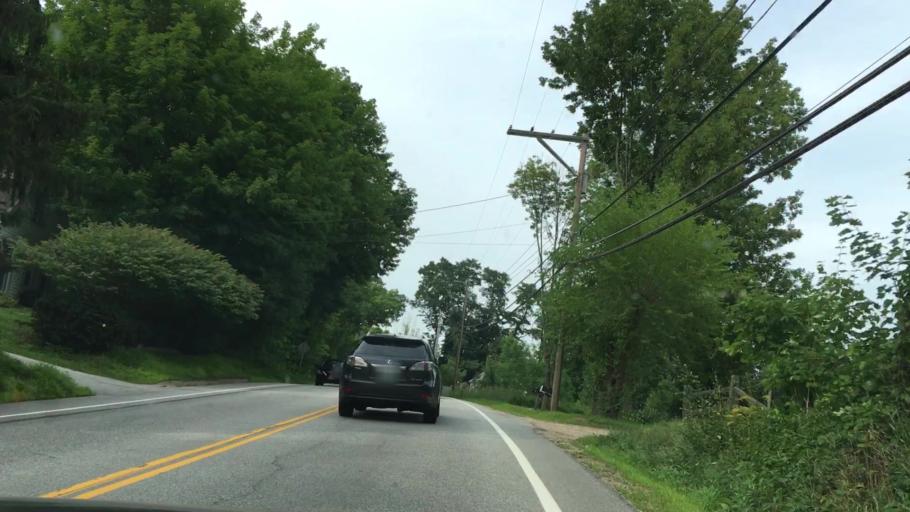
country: US
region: New Hampshire
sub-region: Belknap County
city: Meredith
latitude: 43.6704
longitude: -71.4870
